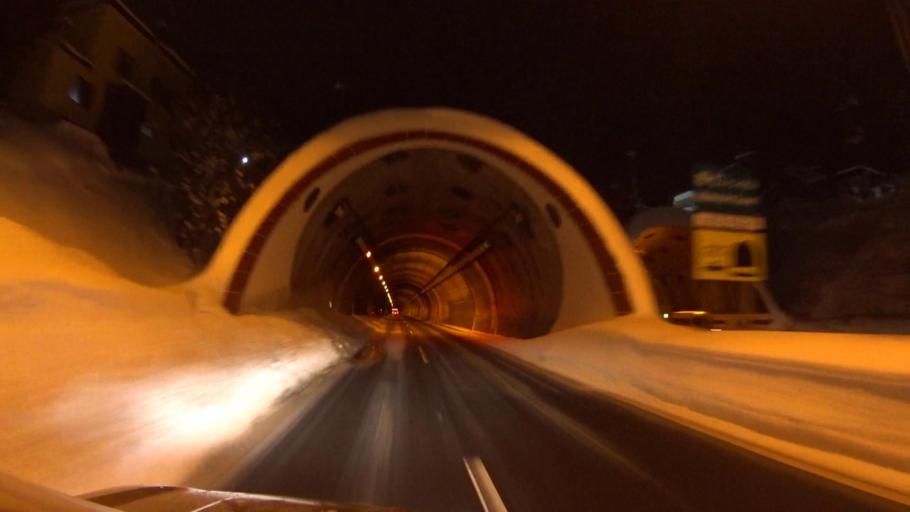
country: JP
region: Hokkaido
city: Otaru
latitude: 43.1764
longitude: 141.0264
